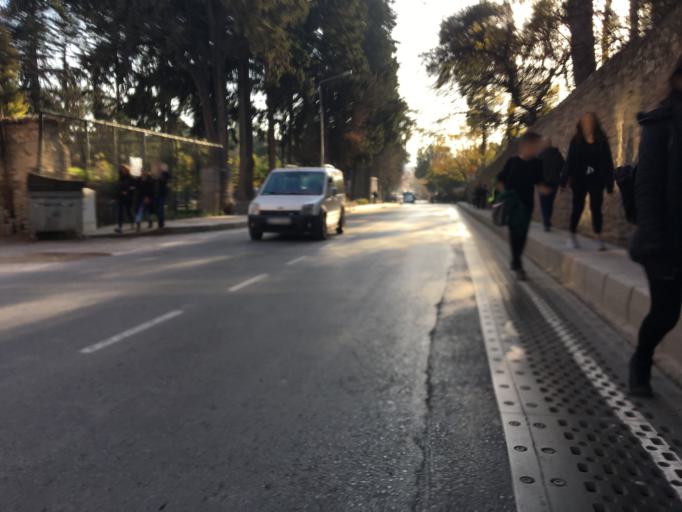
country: TR
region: Izmir
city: Buca
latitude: 38.3845
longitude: 27.1777
